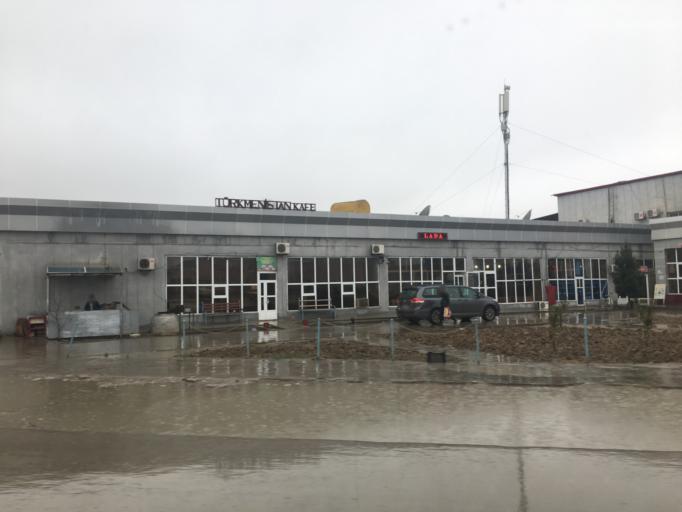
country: TM
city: Murgab
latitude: 37.4967
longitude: 61.9692
